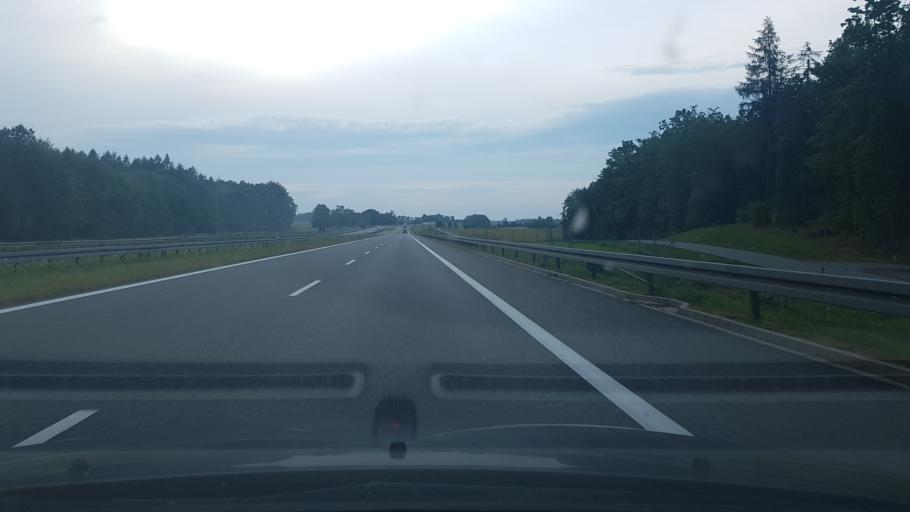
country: PL
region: Warmian-Masurian Voivodeship
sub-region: Powiat ostrodzki
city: Maldyty
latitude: 53.9222
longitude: 19.7170
